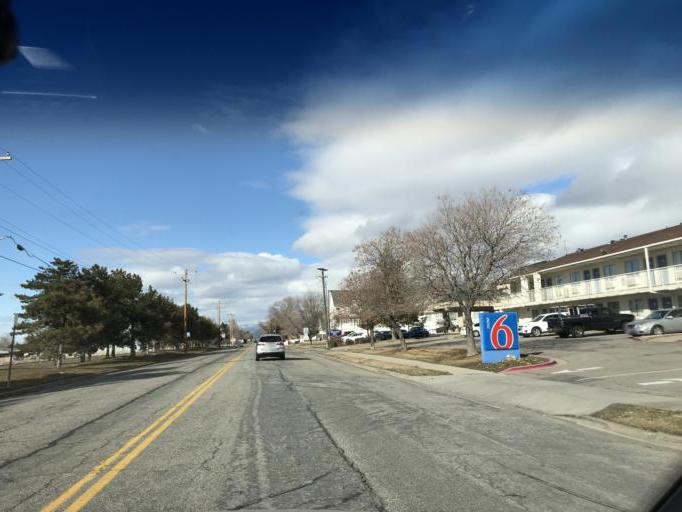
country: US
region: Utah
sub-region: Davis County
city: Woods Cross
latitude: 40.8639
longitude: -111.9021
